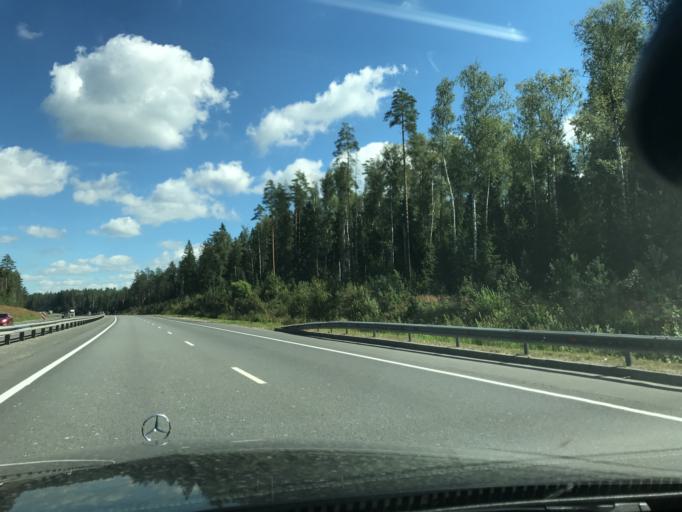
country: RU
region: Vladimir
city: Sudogda
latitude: 56.1453
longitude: 40.9085
